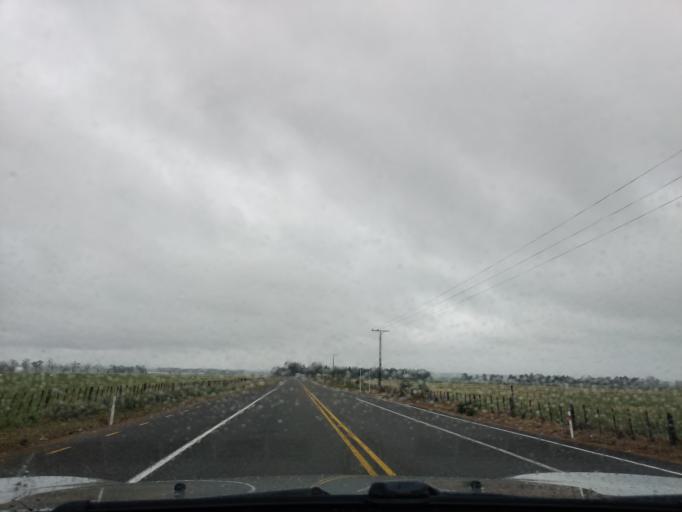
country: NZ
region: Hawke's Bay
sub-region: Hastings District
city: Hastings
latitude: -40.0162
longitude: 176.3565
